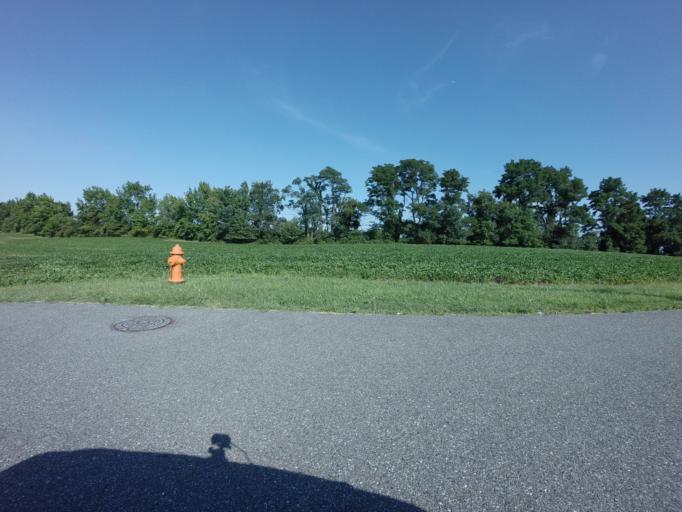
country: US
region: Maryland
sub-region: Baltimore County
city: Edgemere
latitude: 39.2175
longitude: -76.4360
